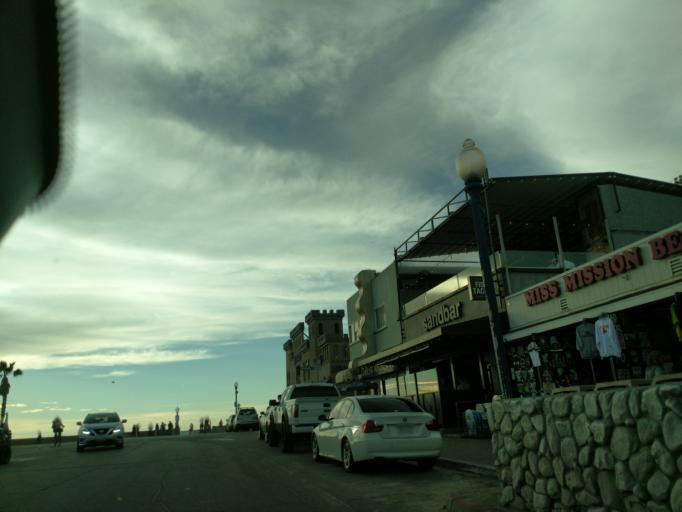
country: US
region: California
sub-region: San Diego County
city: La Jolla
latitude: 32.7721
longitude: -117.2522
